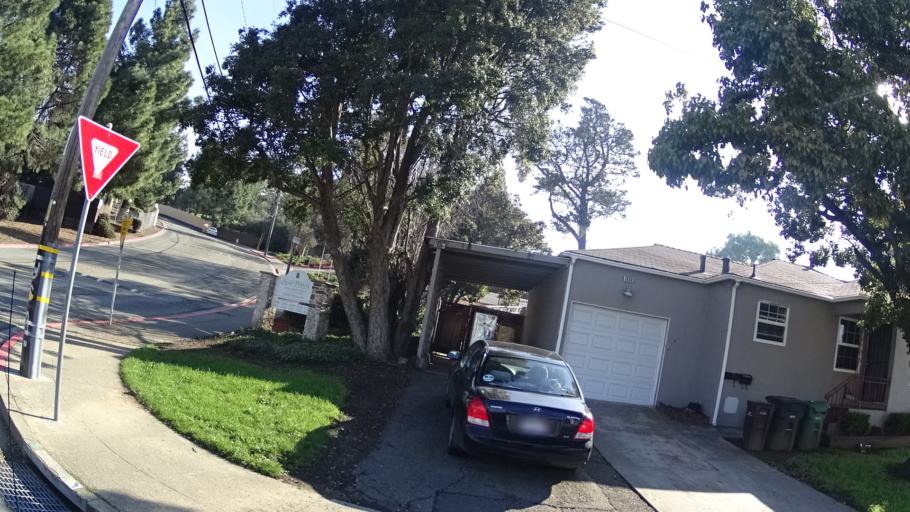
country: US
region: California
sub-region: Alameda County
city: Fairview
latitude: 37.6810
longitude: -122.0636
